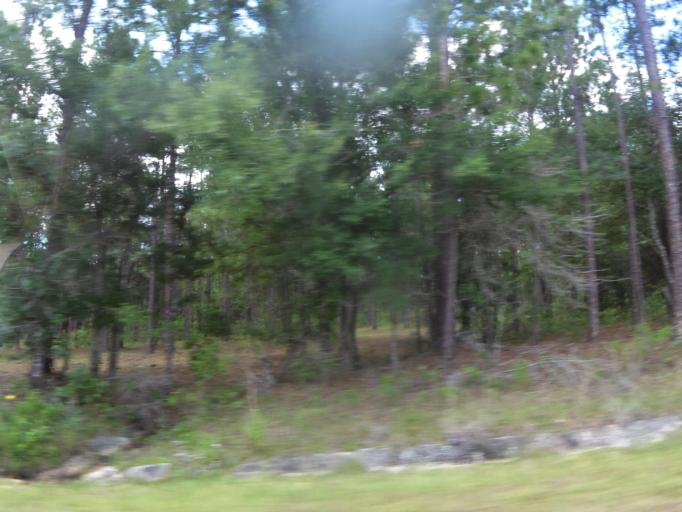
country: US
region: Florida
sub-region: Clay County
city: Asbury Lake
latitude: 29.9091
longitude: -81.8785
